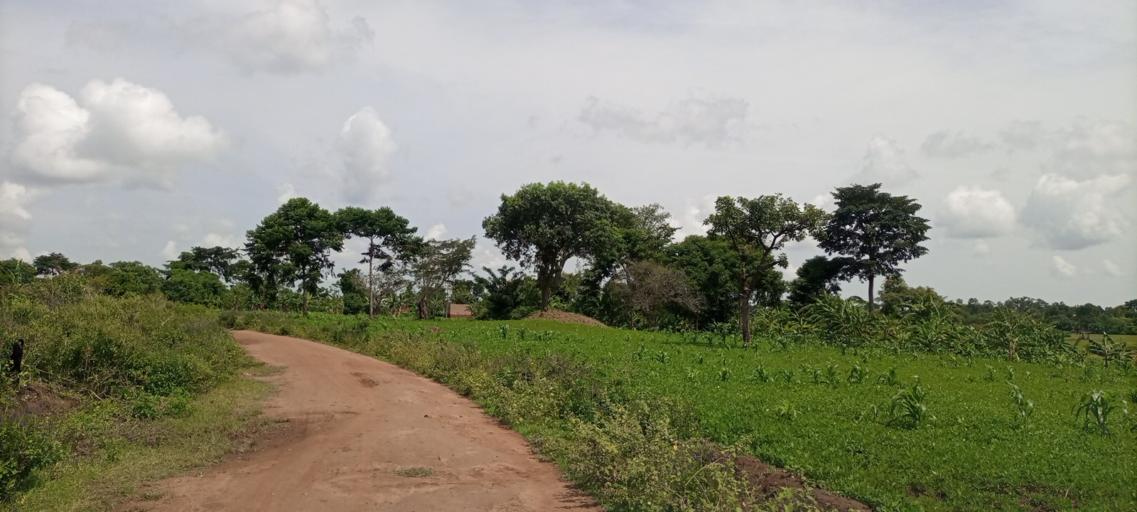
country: UG
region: Eastern Region
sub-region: Budaka District
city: Budaka
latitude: 1.1776
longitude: 33.9174
